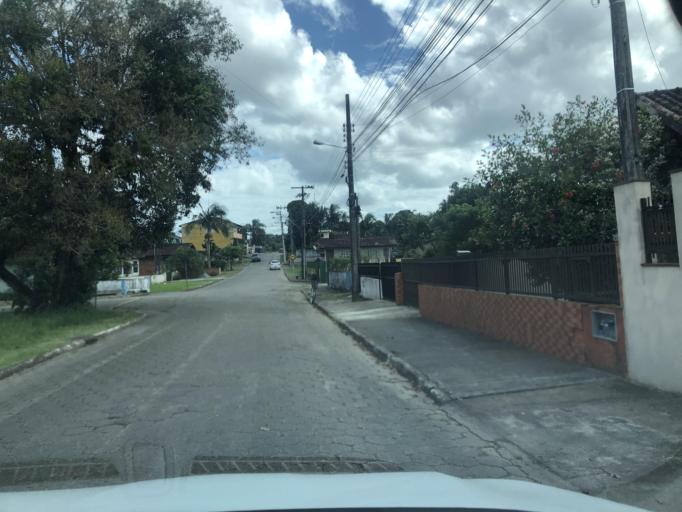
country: BR
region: Santa Catarina
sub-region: Sao Francisco Do Sul
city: Sao Francisco do Sul
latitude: -26.2453
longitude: -48.6277
